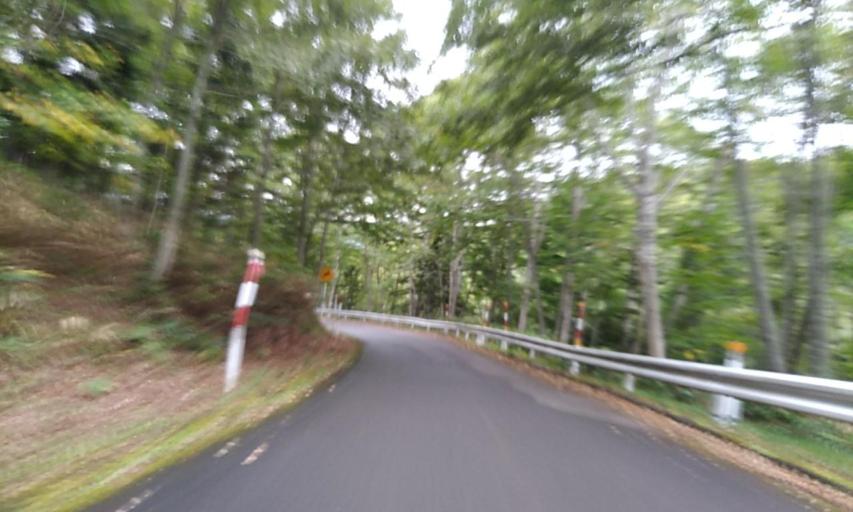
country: JP
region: Hokkaido
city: Bihoro
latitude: 43.5706
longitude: 144.1955
